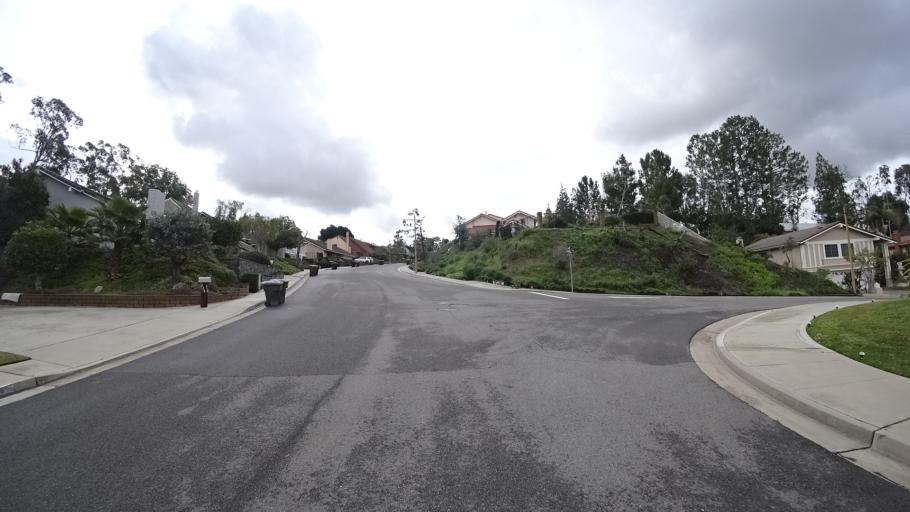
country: US
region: California
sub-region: Orange County
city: Villa Park
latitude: 33.8479
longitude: -117.7805
